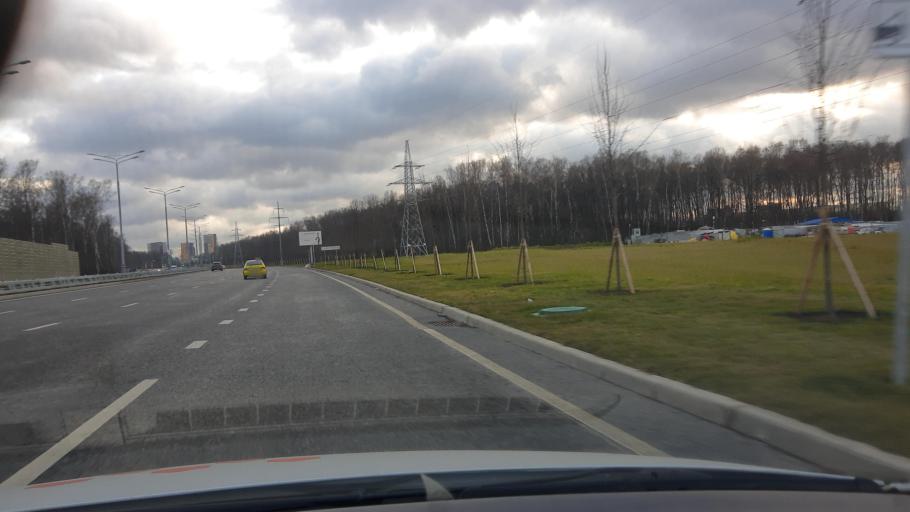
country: RU
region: Moskovskaya
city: Kommunarka
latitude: 55.5930
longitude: 37.4815
